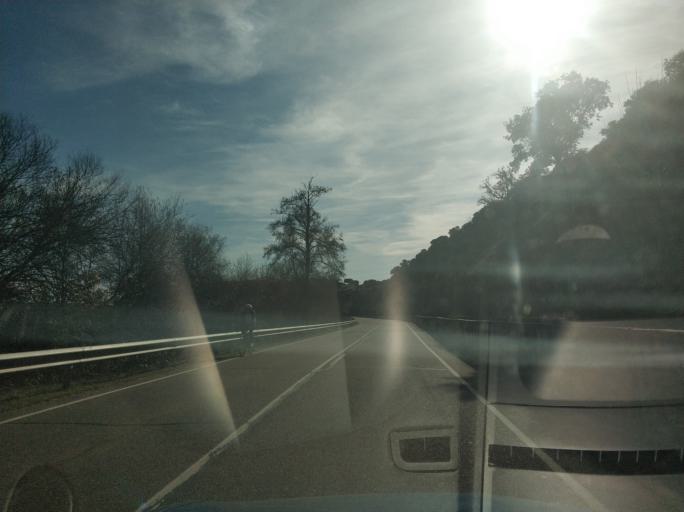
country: ES
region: Castille and Leon
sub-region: Provincia de Salamanca
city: Carrascal de Barregas
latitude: 40.9960
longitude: -5.7326
